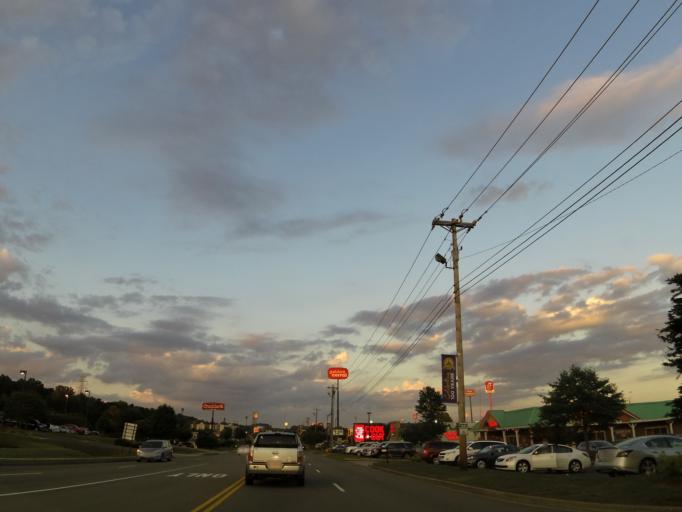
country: US
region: Tennessee
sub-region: Putnam County
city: Cookeville
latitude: 36.1379
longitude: -85.5111
